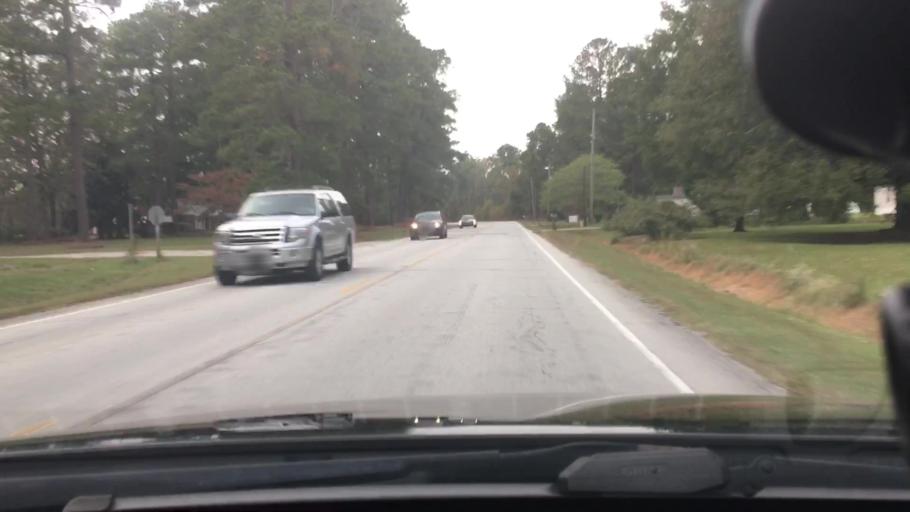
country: US
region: North Carolina
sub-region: Craven County
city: Vanceboro
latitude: 35.4076
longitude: -77.2436
